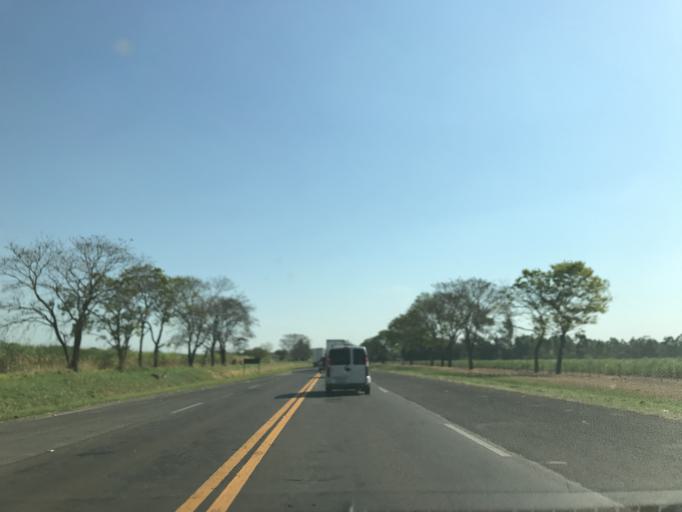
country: BR
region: Sao Paulo
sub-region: Penapolis
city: Penapolis
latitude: -21.4766
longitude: -50.1973
